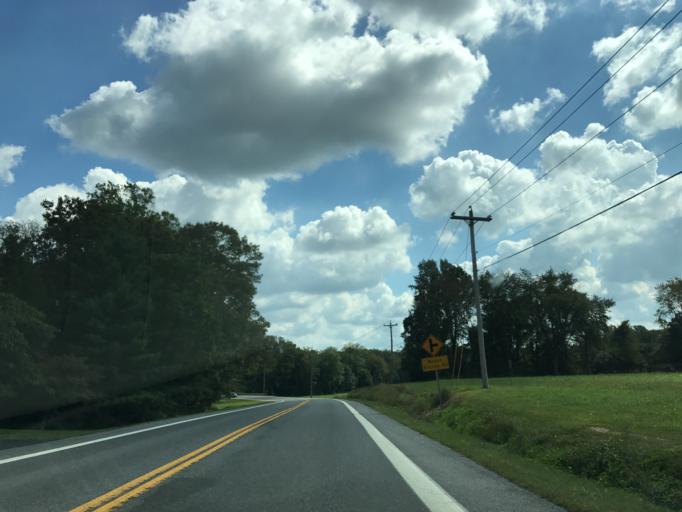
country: US
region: Maryland
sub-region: Caroline County
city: Ridgely
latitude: 39.0099
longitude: -75.9400
